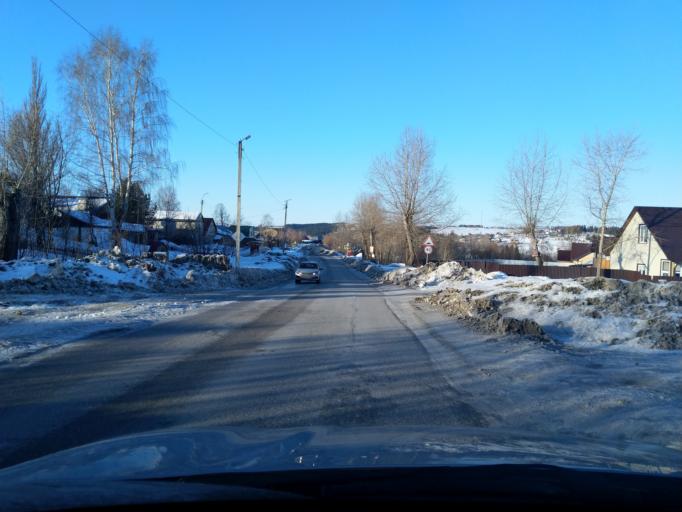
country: RU
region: Perm
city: Polazna
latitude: 58.2945
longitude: 56.4159
